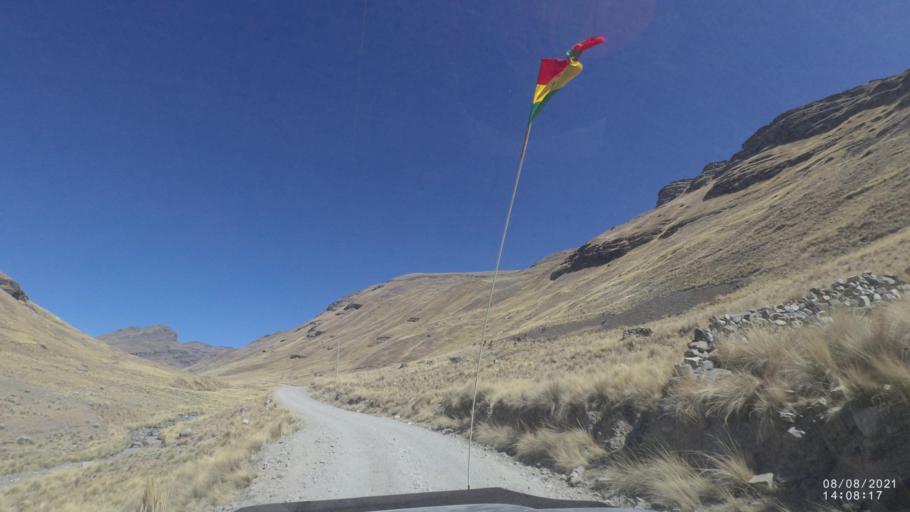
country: BO
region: Cochabamba
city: Sipe Sipe
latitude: -17.1368
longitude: -66.4405
